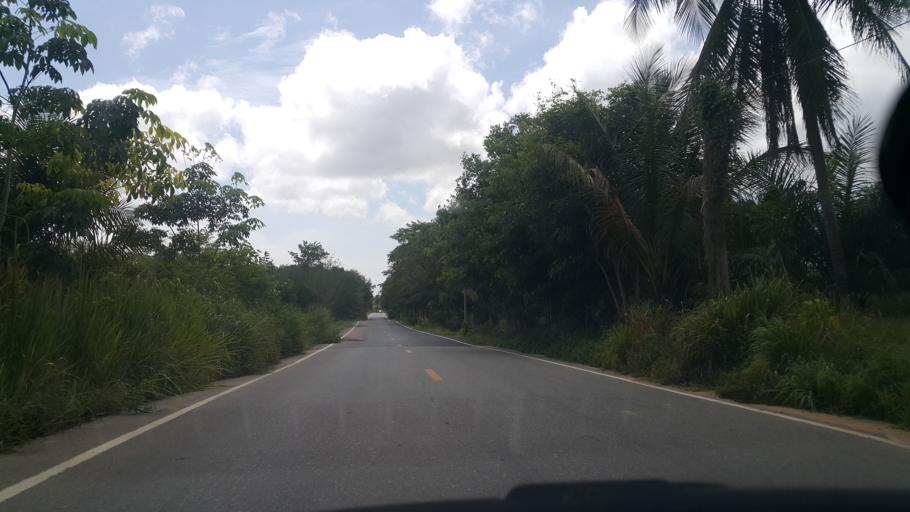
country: TH
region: Rayong
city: Ban Chang
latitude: 12.8018
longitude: 101.0187
